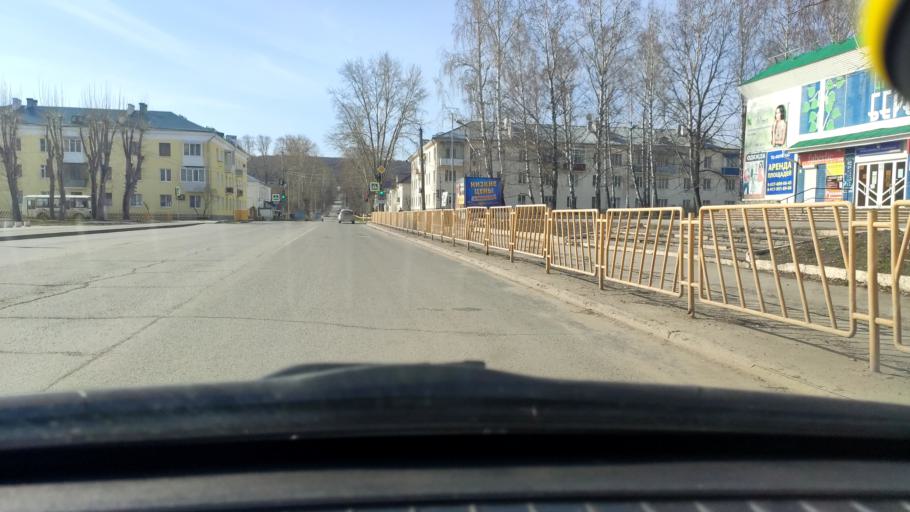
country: RU
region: Samara
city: Zhigulevsk
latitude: 53.4020
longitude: 49.4977
